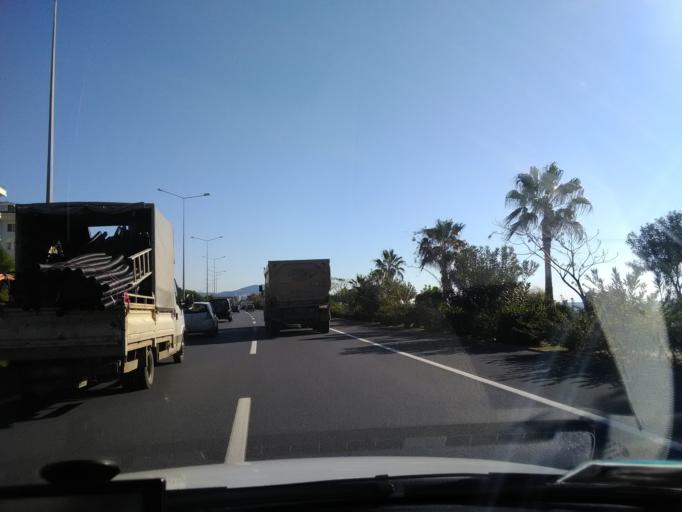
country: TR
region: Antalya
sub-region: Alanya
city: Mahmutlar
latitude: 36.5125
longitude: 32.0660
